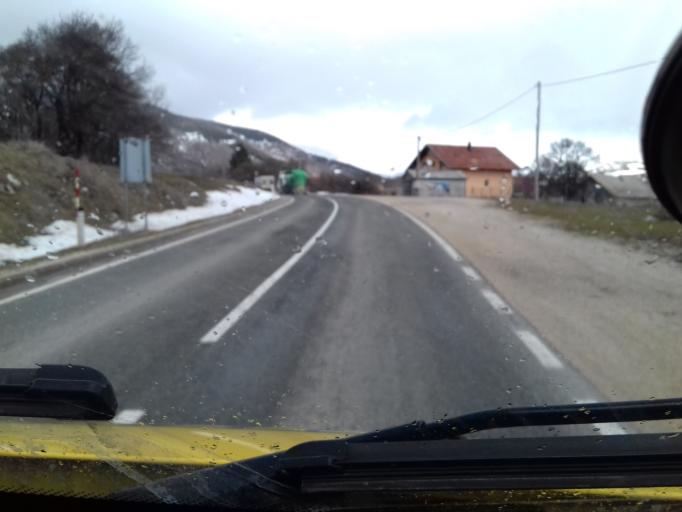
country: BA
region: Federation of Bosnia and Herzegovina
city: Tomislavgrad
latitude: 43.8443
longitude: 17.1731
